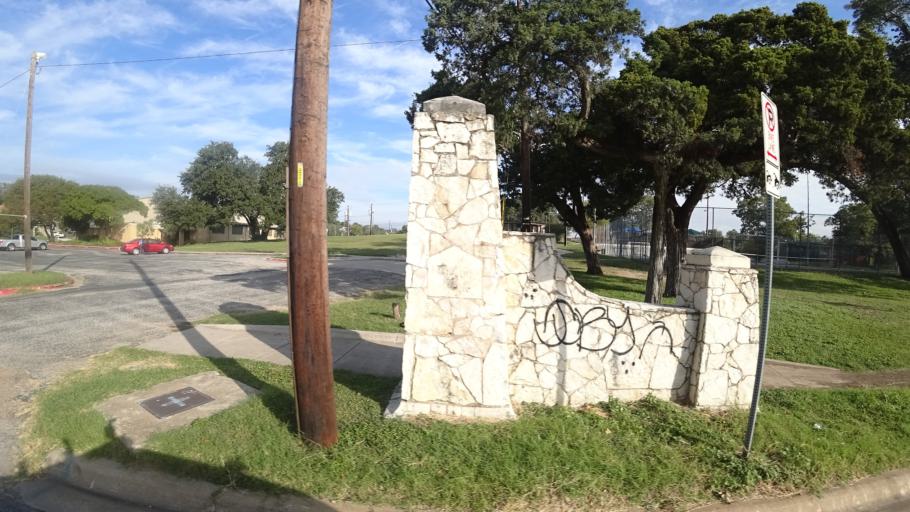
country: US
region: Texas
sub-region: Travis County
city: Austin
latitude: 30.2705
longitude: -97.7141
